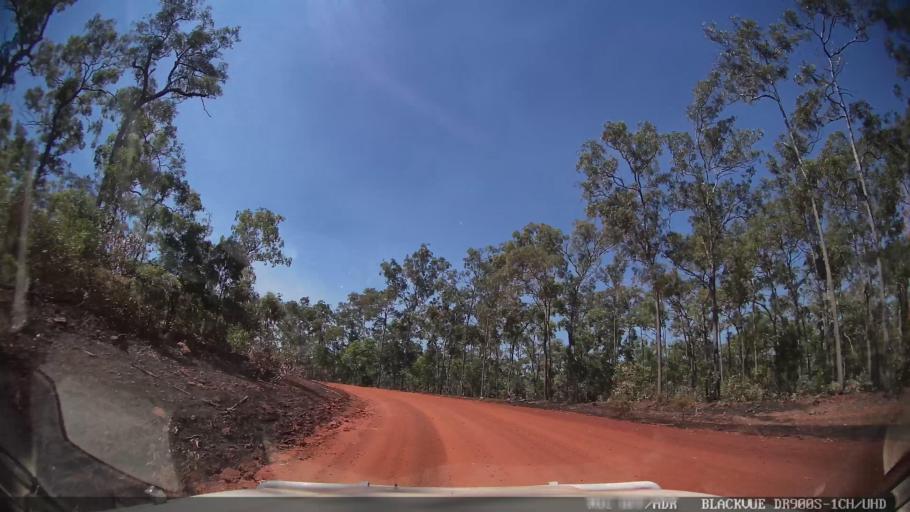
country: AU
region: Queensland
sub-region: Torres
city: Thursday Island
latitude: -10.9740
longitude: 142.3384
